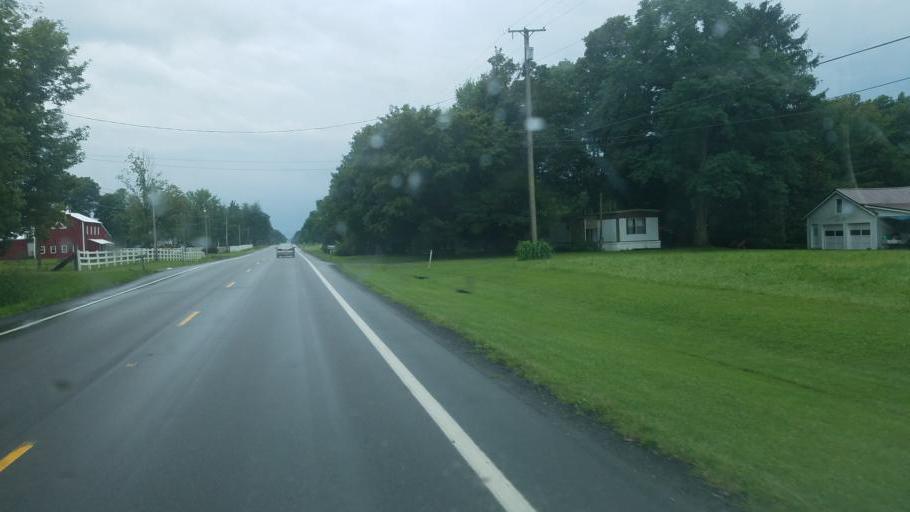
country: US
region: Ohio
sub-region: Ashtabula County
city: Orwell
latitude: 41.4236
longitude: -80.8689
